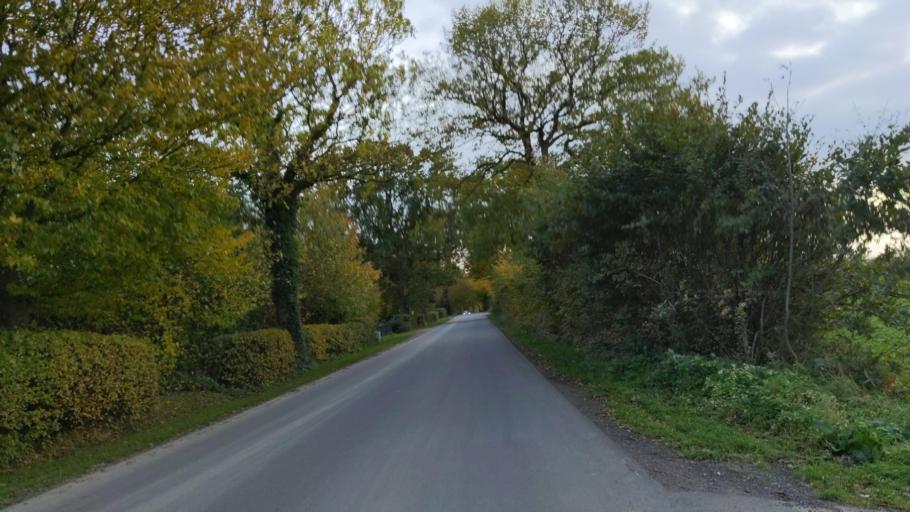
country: DE
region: Schleswig-Holstein
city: Sierksdorf
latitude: 54.0800
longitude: 10.7439
